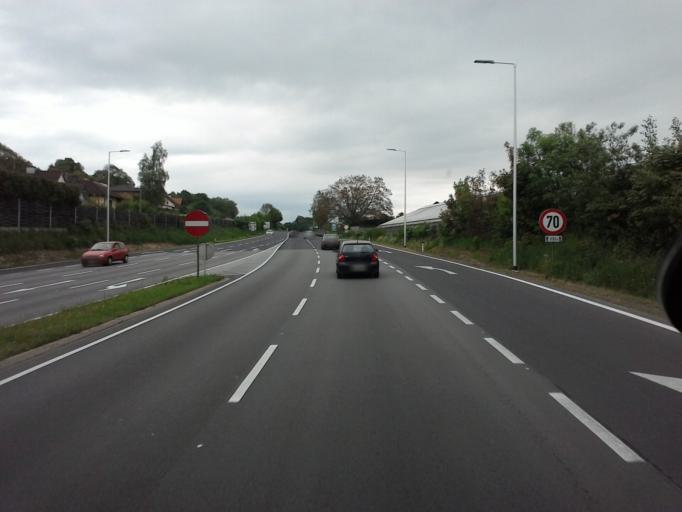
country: AT
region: Upper Austria
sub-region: Wels-Land
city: Thalheim bei Wels
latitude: 48.1509
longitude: 14.0441
